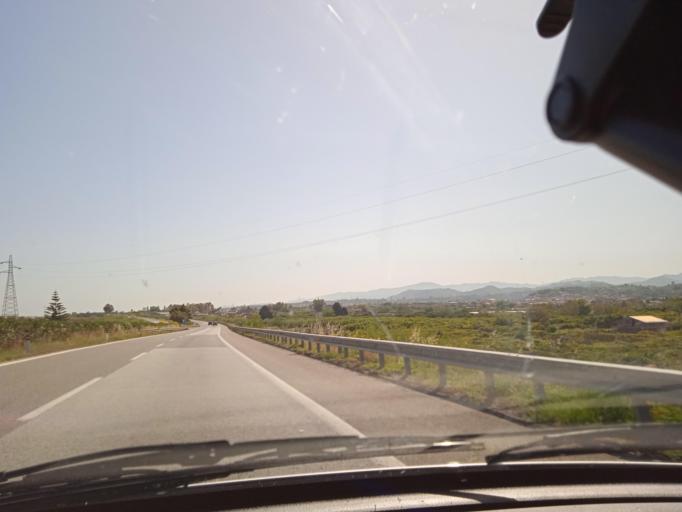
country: IT
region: Sicily
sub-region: Messina
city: Barcellona Pozzo di Gotto
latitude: 38.1709
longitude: 15.2285
